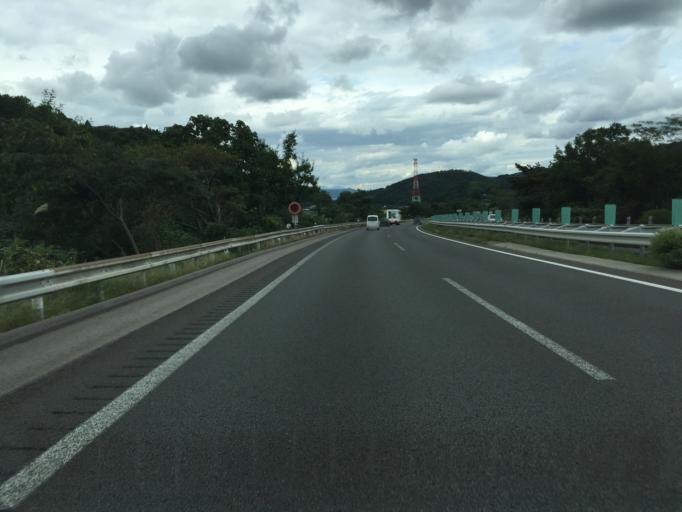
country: JP
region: Miyagi
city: Shiroishi
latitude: 37.9514
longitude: 140.6165
